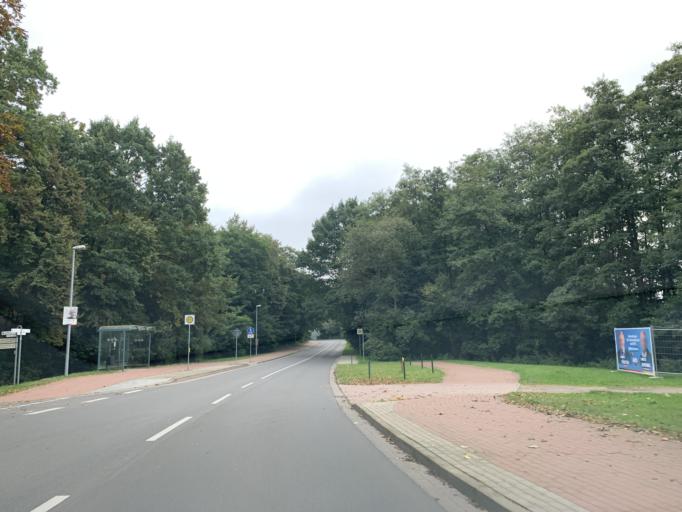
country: DE
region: Mecklenburg-Vorpommern
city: Loitz
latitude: 53.3416
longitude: 13.4552
